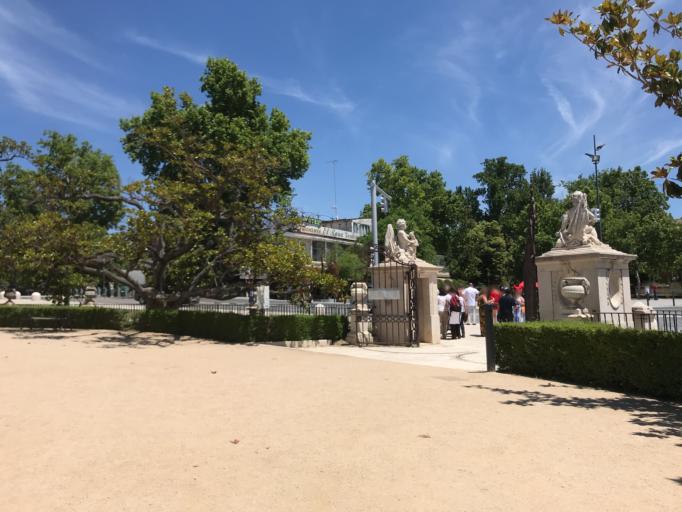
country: ES
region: Madrid
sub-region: Provincia de Madrid
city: Aranjuez
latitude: 40.0360
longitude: -3.6053
